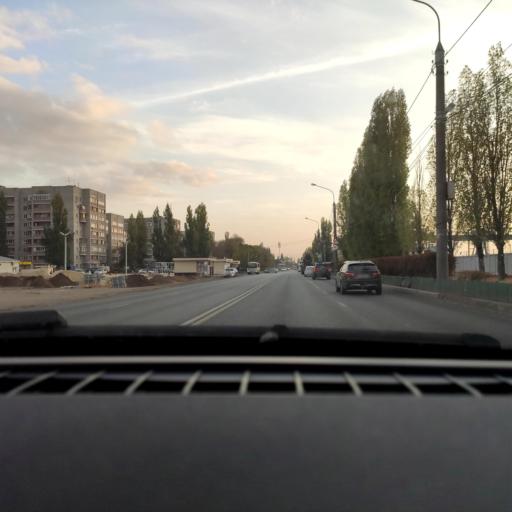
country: RU
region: Voronezj
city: Voronezh
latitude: 51.6428
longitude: 39.2665
